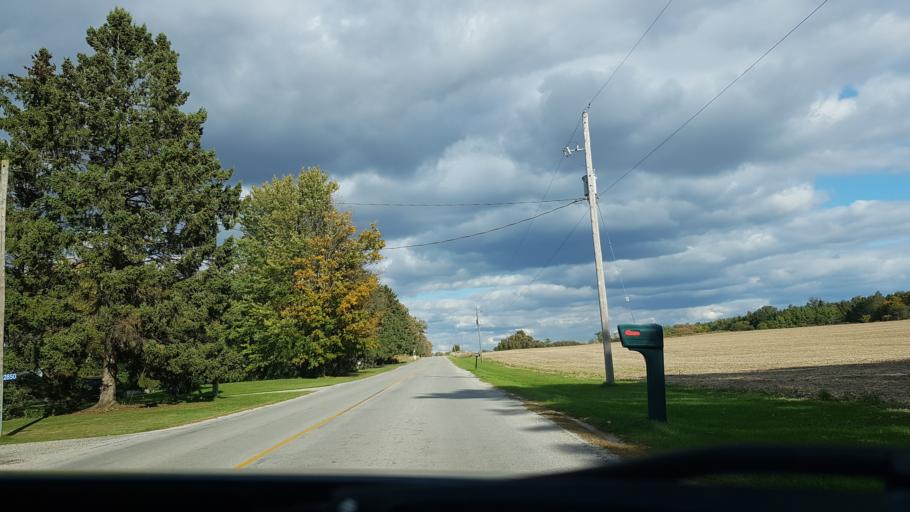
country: CA
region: Ontario
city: Delaware
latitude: 43.0062
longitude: -81.3982
